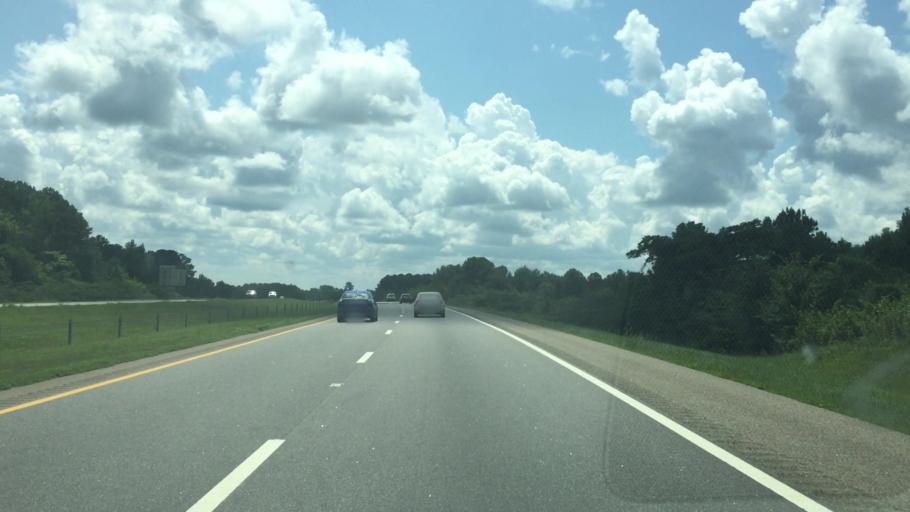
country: US
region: North Carolina
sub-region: Richmond County
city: Cordova
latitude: 34.9363
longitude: -79.8397
